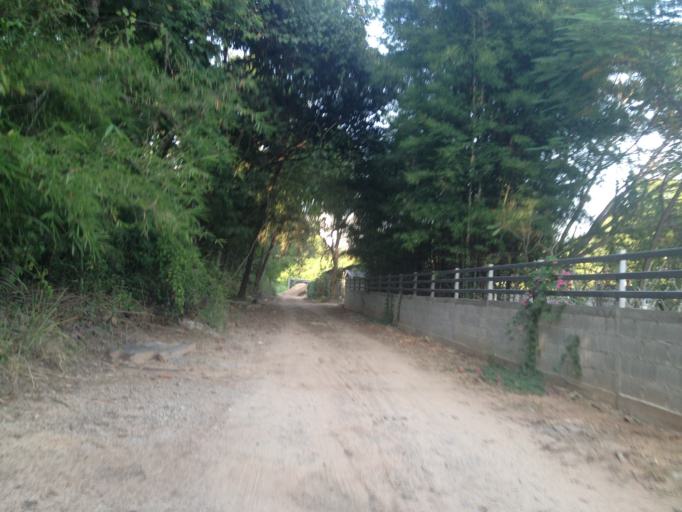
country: TH
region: Chiang Mai
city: Hang Dong
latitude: 18.7378
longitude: 98.9232
